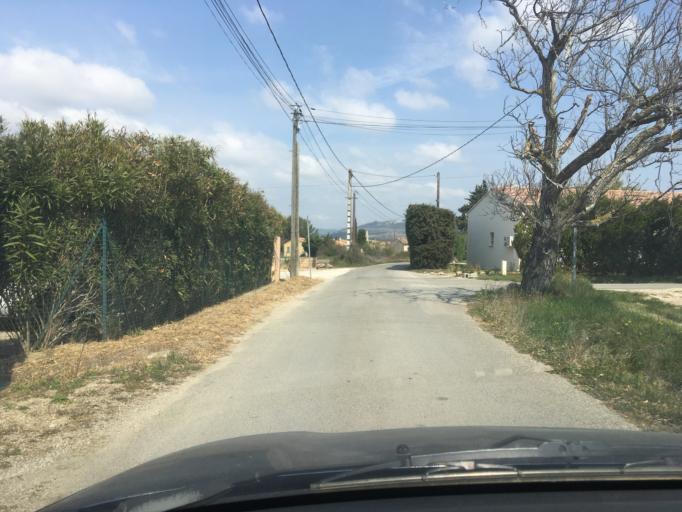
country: FR
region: Provence-Alpes-Cote d'Azur
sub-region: Departement du Vaucluse
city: Aubignan
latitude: 44.0907
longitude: 5.0159
